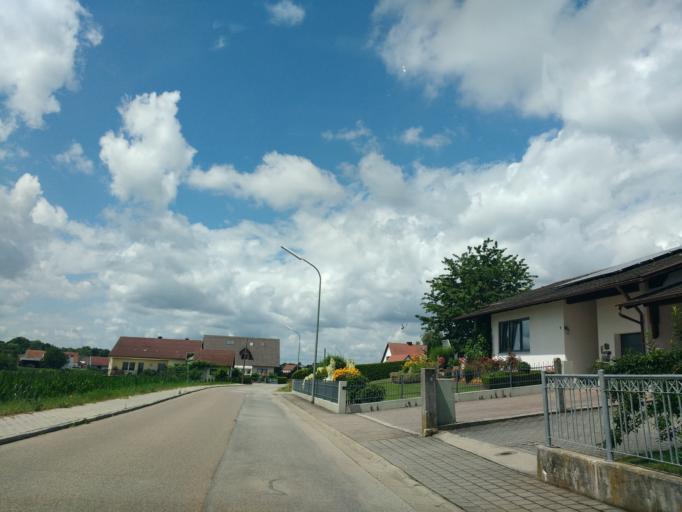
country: DE
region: Bavaria
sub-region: Upper Bavaria
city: Rohrbach
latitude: 48.6512
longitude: 11.5339
